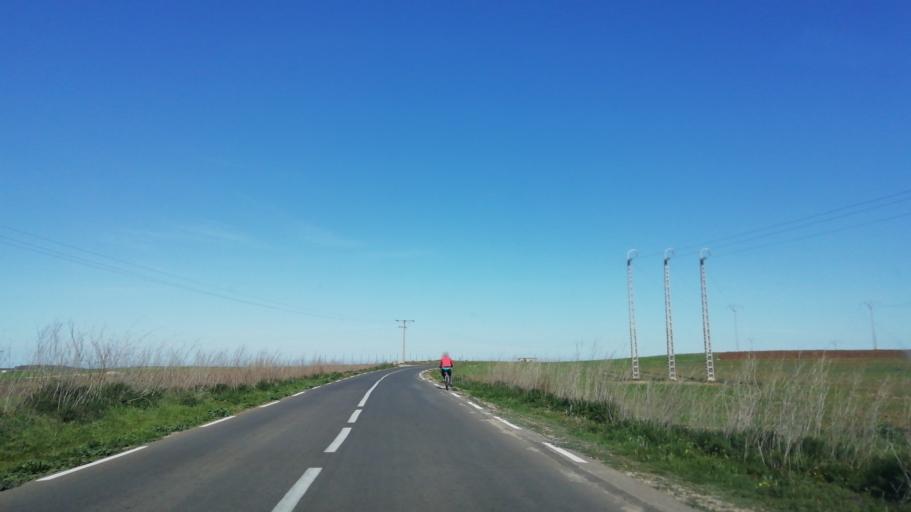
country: DZ
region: Oran
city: Bou Tlelis
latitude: 35.6440
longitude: -0.9450
